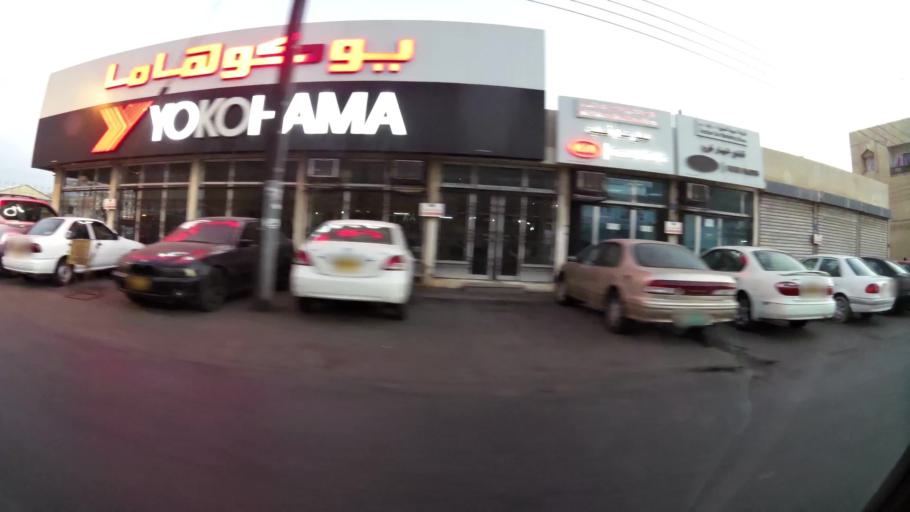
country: OM
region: Muhafazat Masqat
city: Muscat
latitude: 23.5917
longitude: 58.5615
